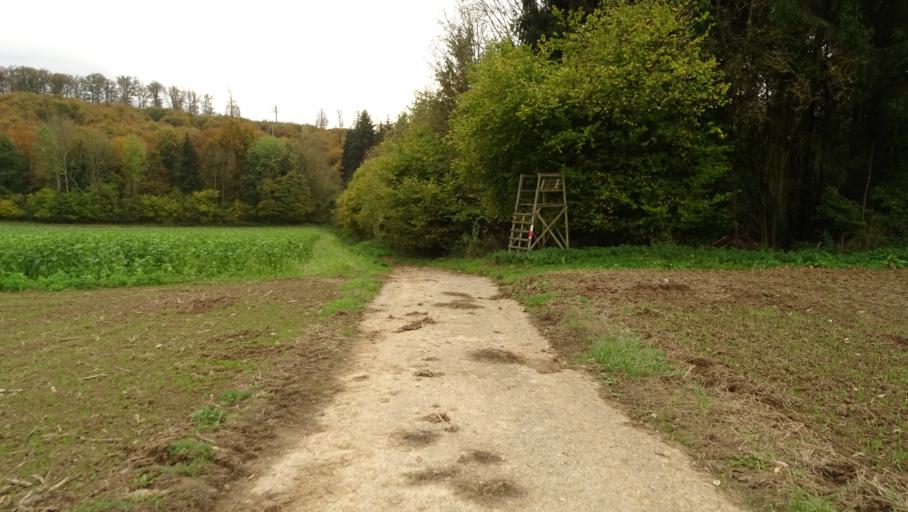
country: DE
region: Baden-Wuerttemberg
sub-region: Karlsruhe Region
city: Neckargerach
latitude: 49.3842
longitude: 9.0909
